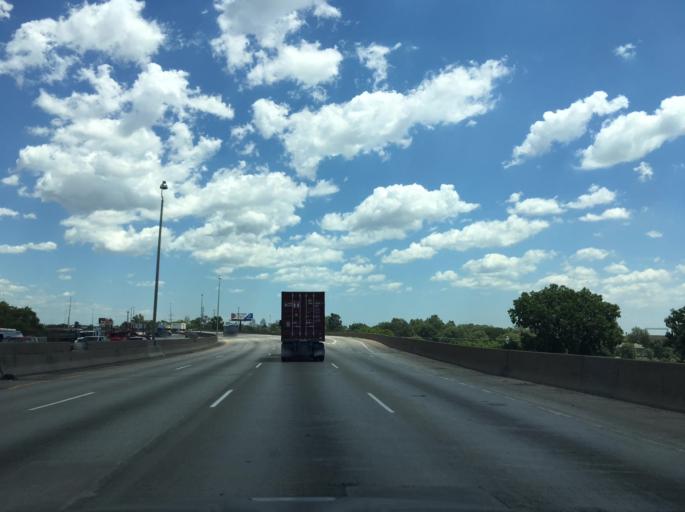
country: US
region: Michigan
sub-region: Wayne County
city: River Rouge
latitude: 42.2900
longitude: -83.1316
